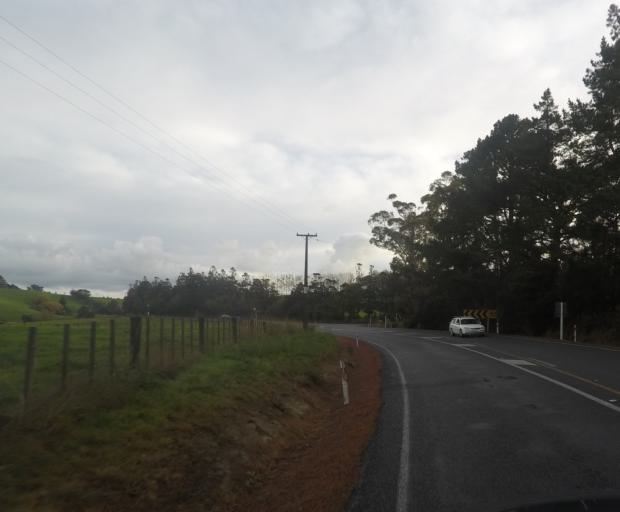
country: NZ
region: Auckland
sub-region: Auckland
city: Wellsford
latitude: -36.1780
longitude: 174.5832
